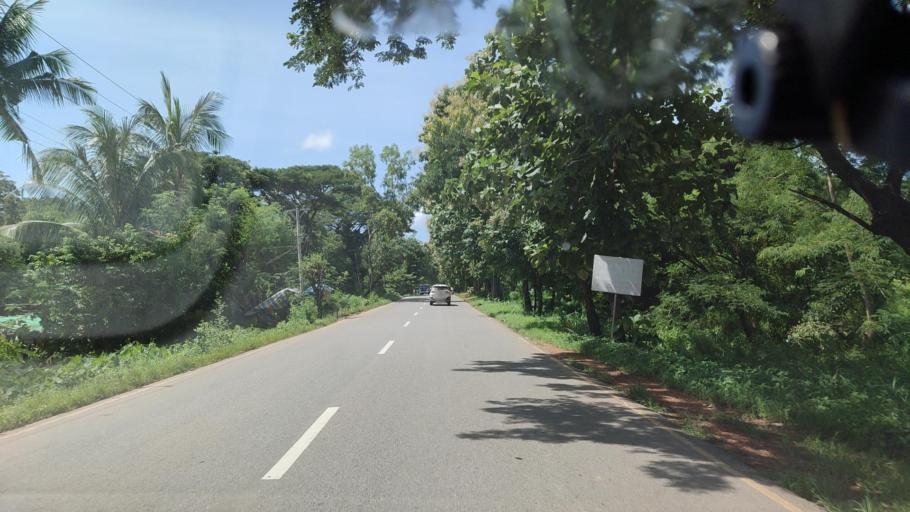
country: MM
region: Bago
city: Paungde
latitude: 18.2650
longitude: 95.6413
